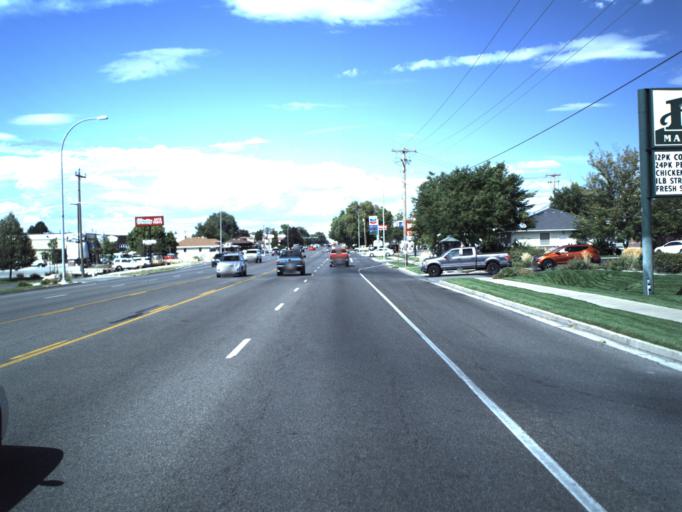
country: US
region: Utah
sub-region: Cache County
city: Smithfield
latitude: 41.8188
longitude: -111.8330
